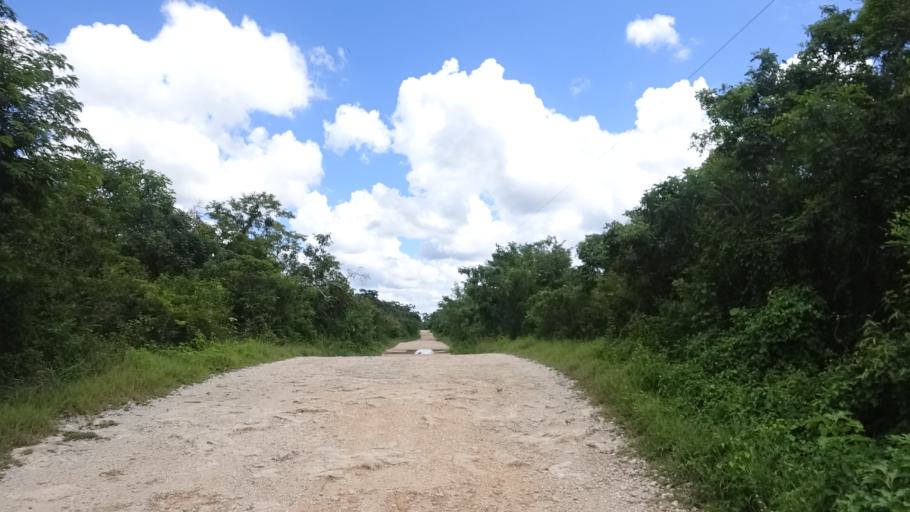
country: MX
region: Yucatan
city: Valladolid
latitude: 20.6737
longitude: -88.2238
